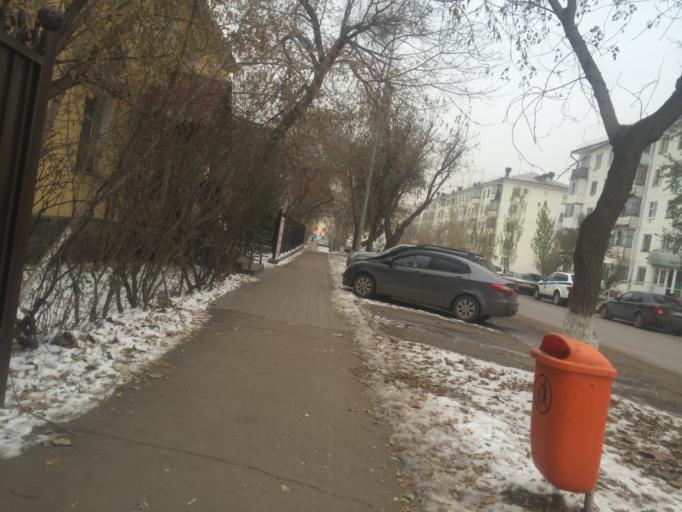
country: KZ
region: Astana Qalasy
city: Astana
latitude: 51.1848
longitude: 71.4193
